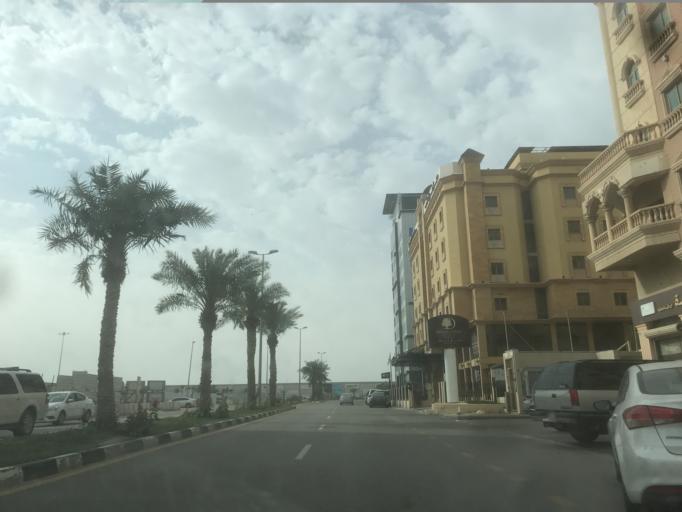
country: SA
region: Eastern Province
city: Khobar
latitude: 26.3036
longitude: 50.1753
